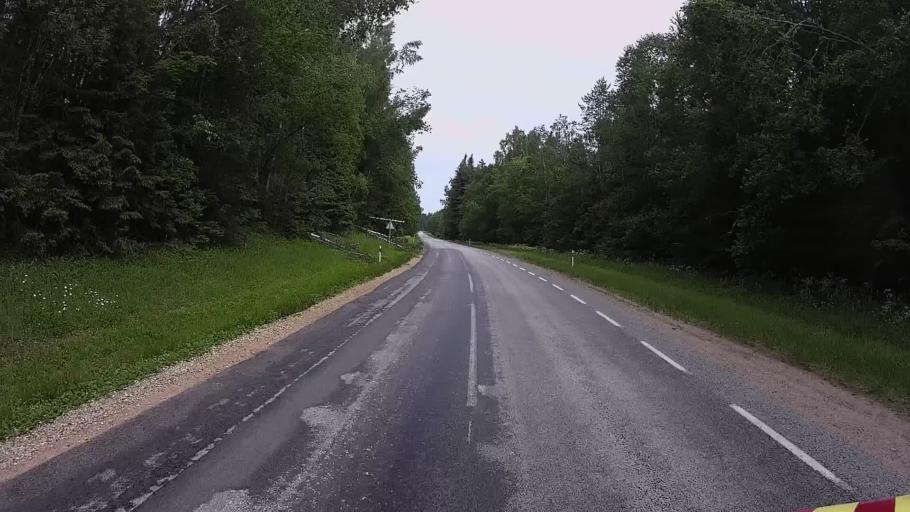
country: EE
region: Viljandimaa
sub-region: Karksi vald
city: Karksi-Nuia
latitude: 58.2101
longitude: 25.6213
